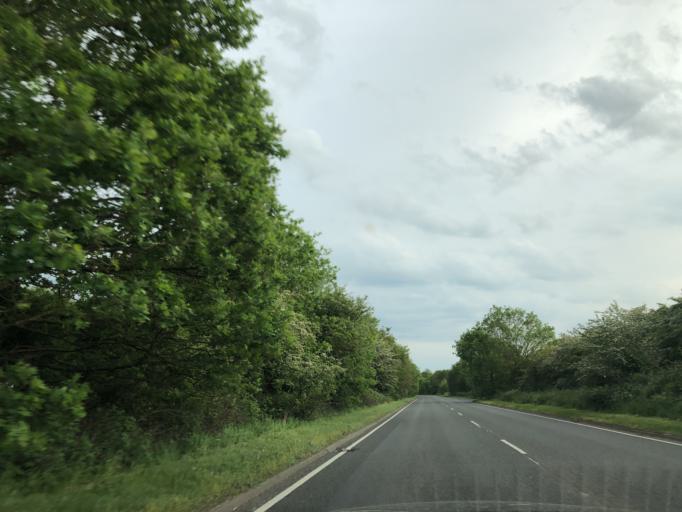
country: GB
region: England
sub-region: Warwickshire
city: Wroxall
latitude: 52.3435
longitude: -1.6557
